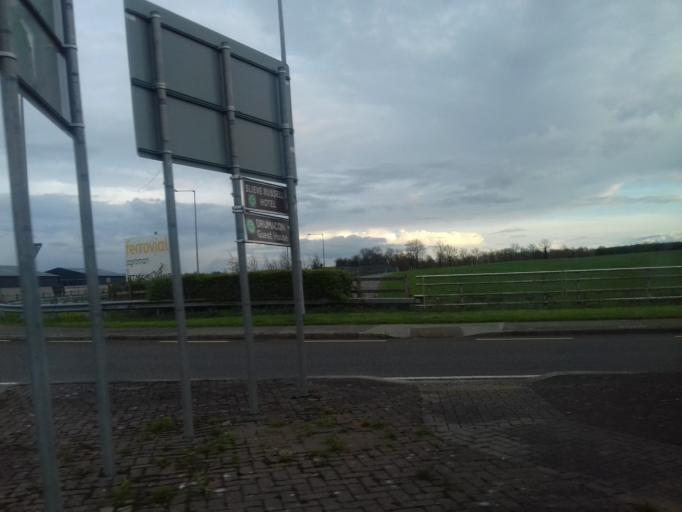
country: IE
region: Ulster
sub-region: An Cabhan
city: Belturbet
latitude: 54.0982
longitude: -7.4611
